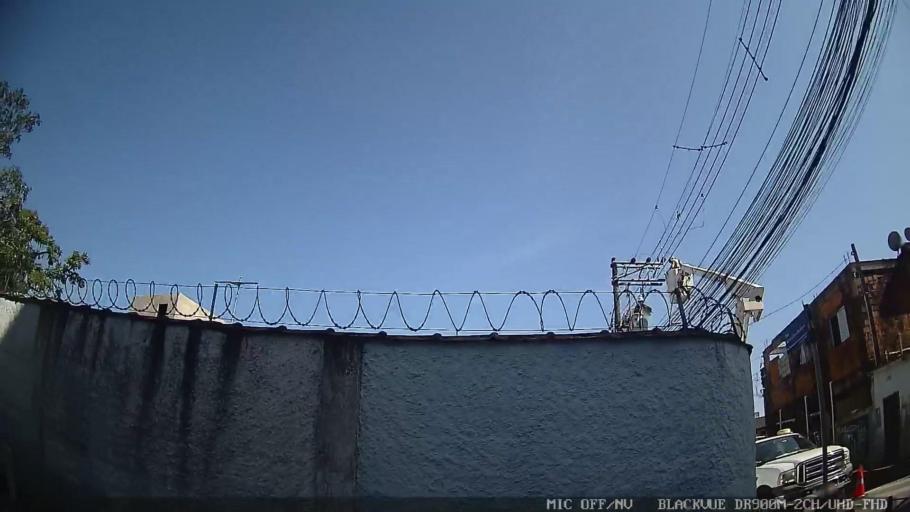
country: BR
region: Sao Paulo
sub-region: Guaruja
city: Guaruja
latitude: -23.9973
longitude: -46.3009
